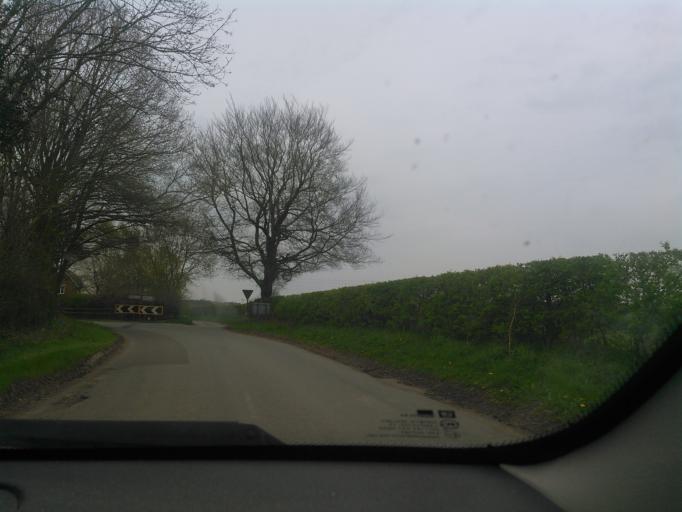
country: GB
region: England
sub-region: Shropshire
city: Shawbury
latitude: 52.8059
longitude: -2.6086
